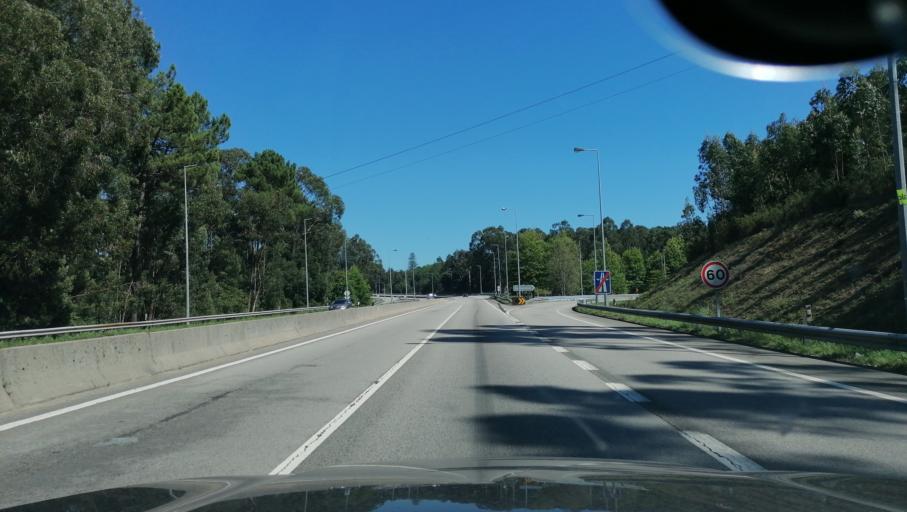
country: PT
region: Aveiro
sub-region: Santa Maria da Feira
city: Rio Meao
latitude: 40.9253
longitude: -8.5821
